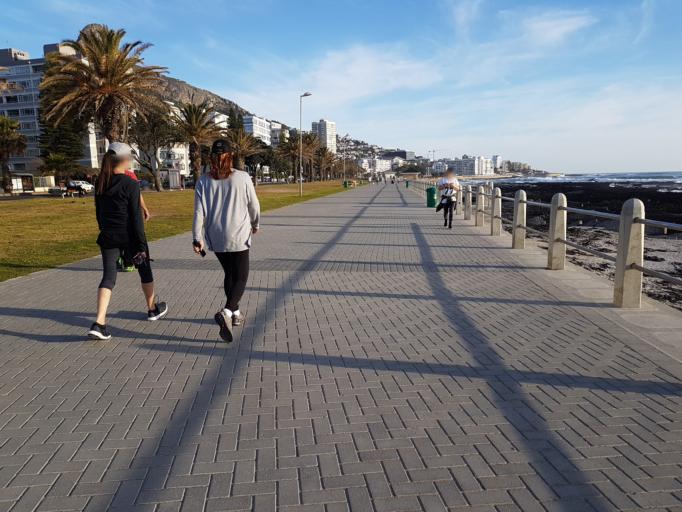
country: ZA
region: Western Cape
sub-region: City of Cape Town
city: Cape Town
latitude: -33.9126
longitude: 18.3881
